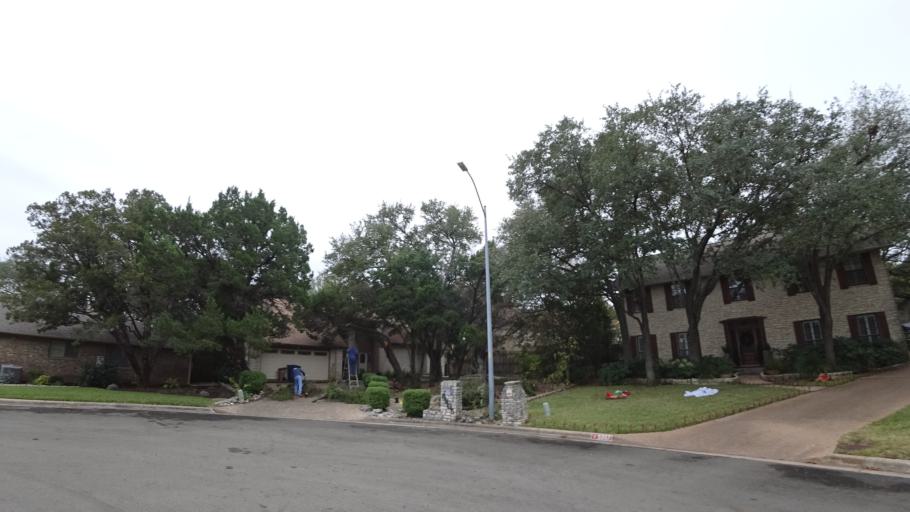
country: US
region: Texas
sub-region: Williamson County
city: Jollyville
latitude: 30.3753
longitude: -97.7960
